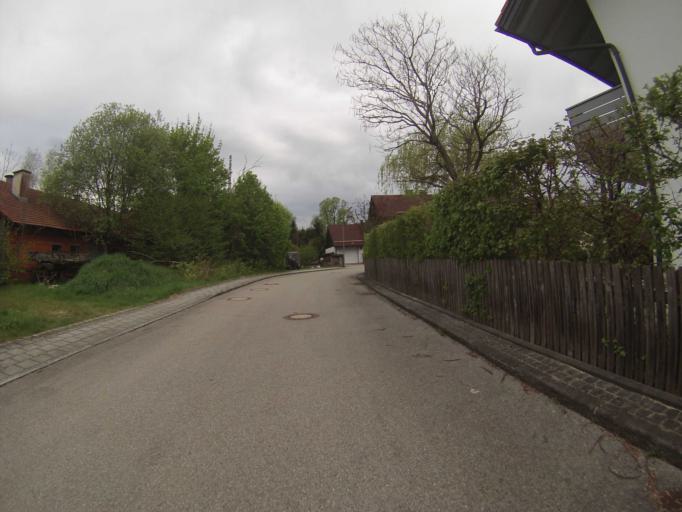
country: DE
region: Bavaria
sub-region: Upper Bavaria
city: Sauerlach
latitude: 47.9759
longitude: 11.6490
